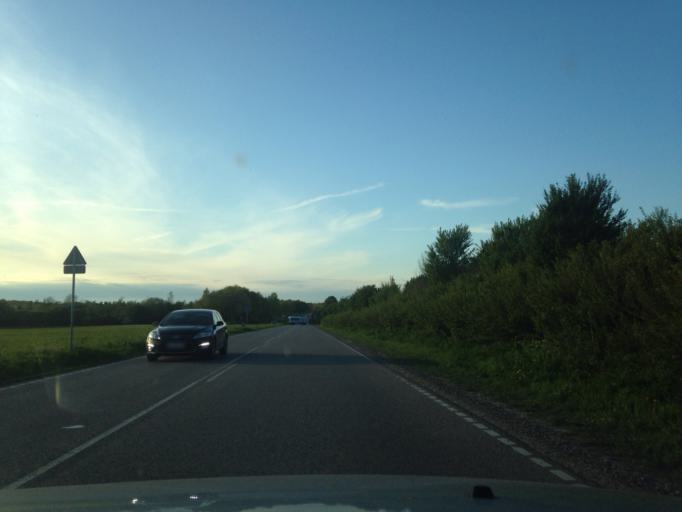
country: DK
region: Capital Region
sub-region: Hoje-Taastrup Kommune
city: Flong
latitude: 55.6372
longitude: 12.1938
